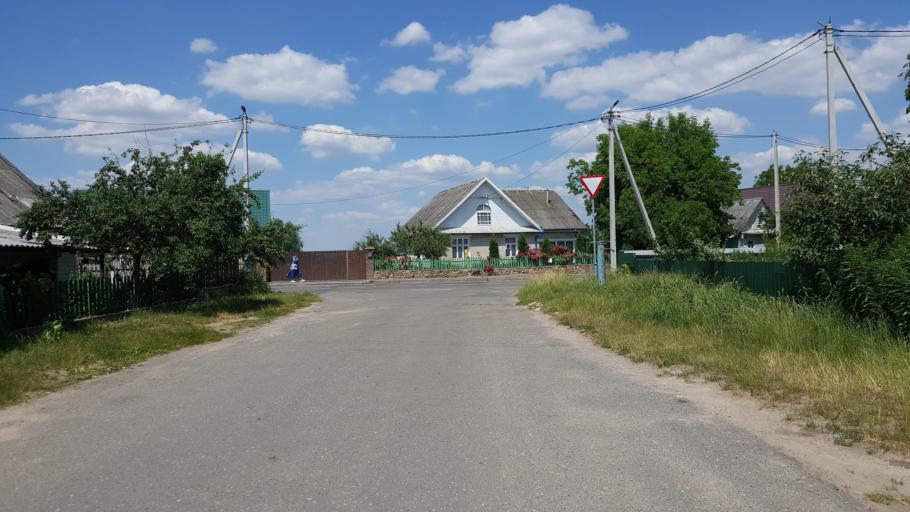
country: BY
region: Brest
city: Kamyanyets
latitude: 52.4038
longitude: 23.8156
